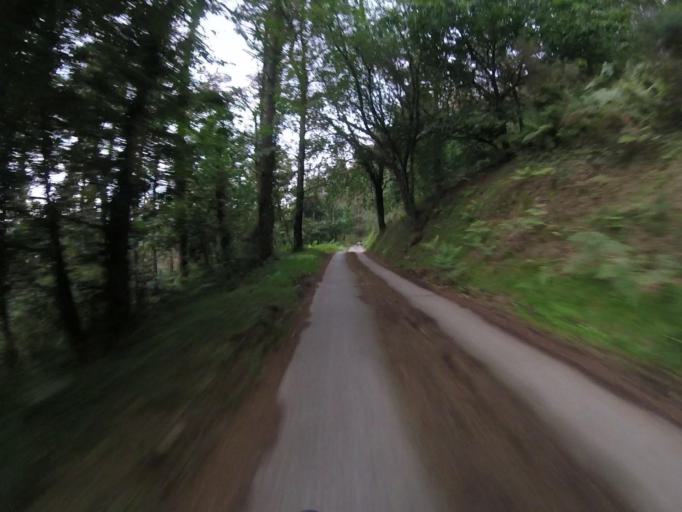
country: ES
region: Basque Country
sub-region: Provincia de Guipuzcoa
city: Errenteria
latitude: 43.2674
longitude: -1.8338
